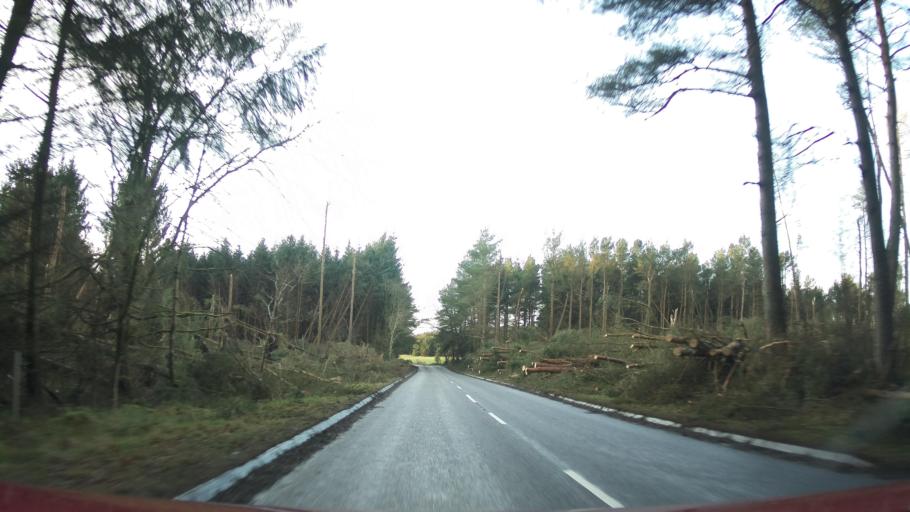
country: GB
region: Scotland
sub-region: Angus
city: Letham
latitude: 56.5856
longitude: -2.8366
